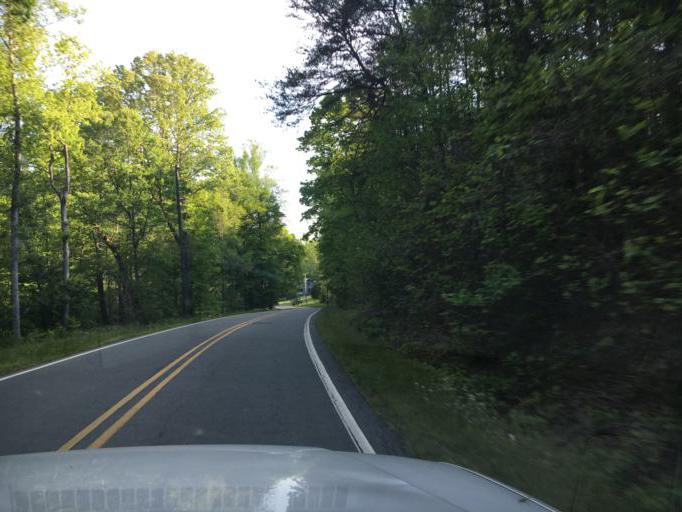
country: US
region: North Carolina
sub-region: Rutherford County
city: Rutherfordton
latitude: 35.2980
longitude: -82.0058
